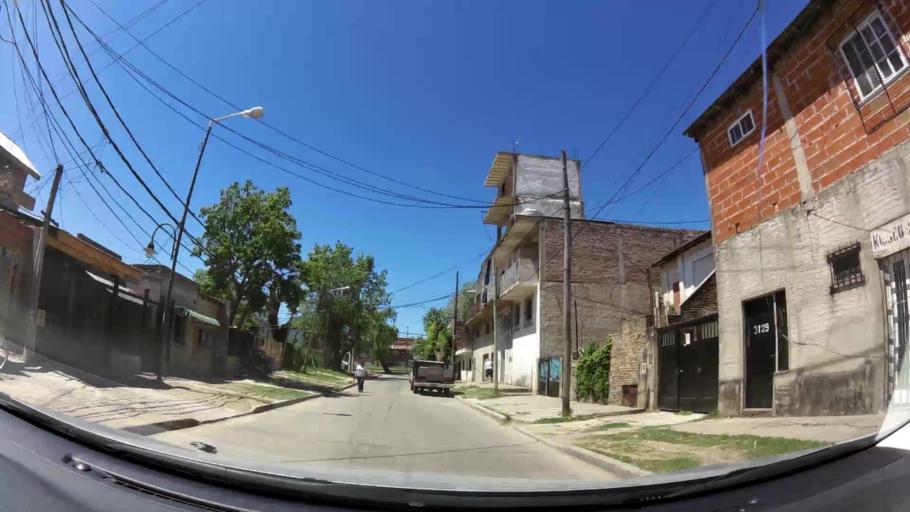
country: AR
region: Buenos Aires
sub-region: Partido de Tigre
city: Tigre
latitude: -34.4608
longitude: -58.5529
